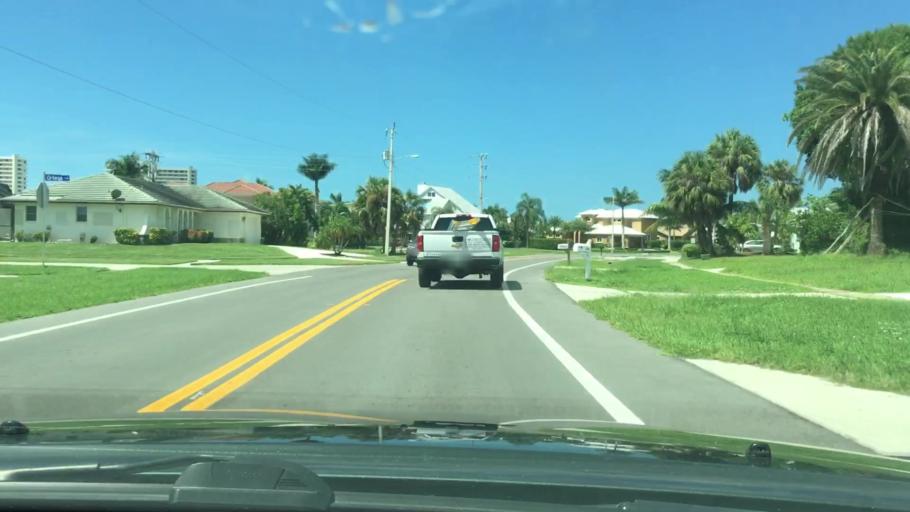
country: US
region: Florida
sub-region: Collier County
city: Marco
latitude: 25.9478
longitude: -81.7332
